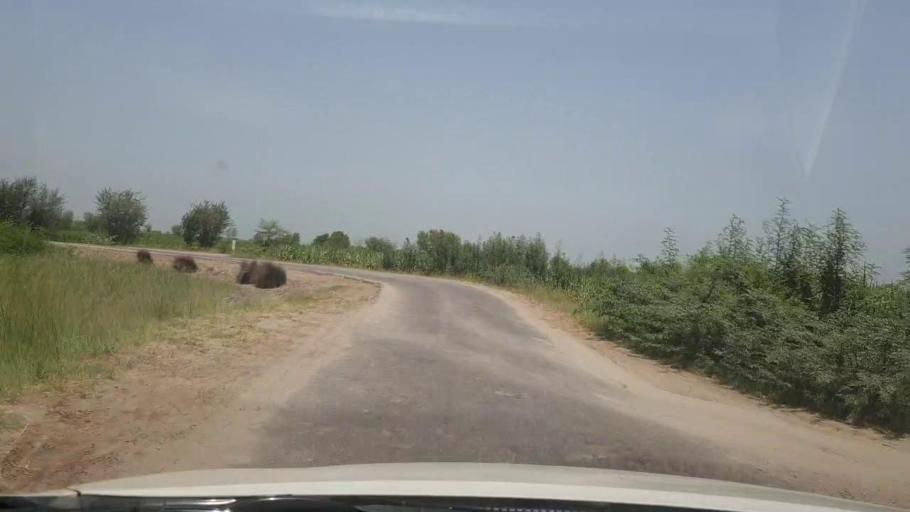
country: PK
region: Sindh
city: Bozdar
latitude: 27.2558
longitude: 68.6381
